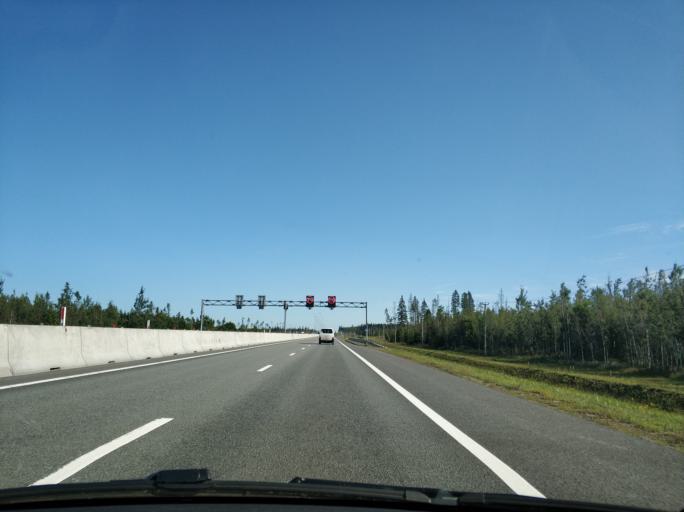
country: RU
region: Leningrad
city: Sosnovo
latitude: 60.4699
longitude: 30.1961
